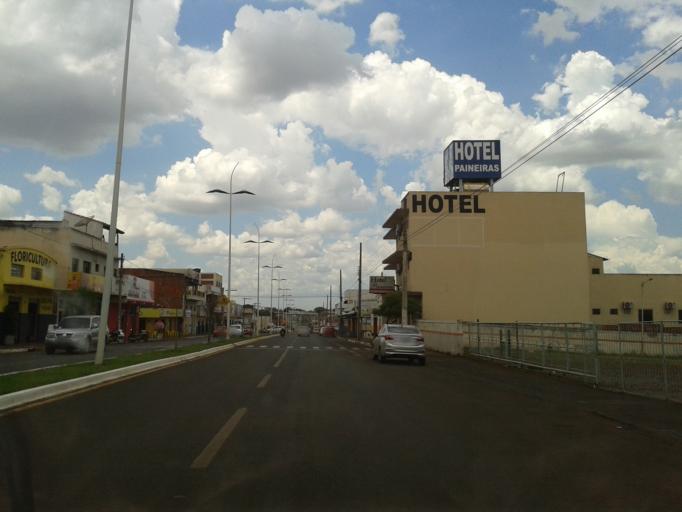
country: BR
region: Goias
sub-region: Itumbiara
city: Itumbiara
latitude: -18.4048
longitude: -49.2095
